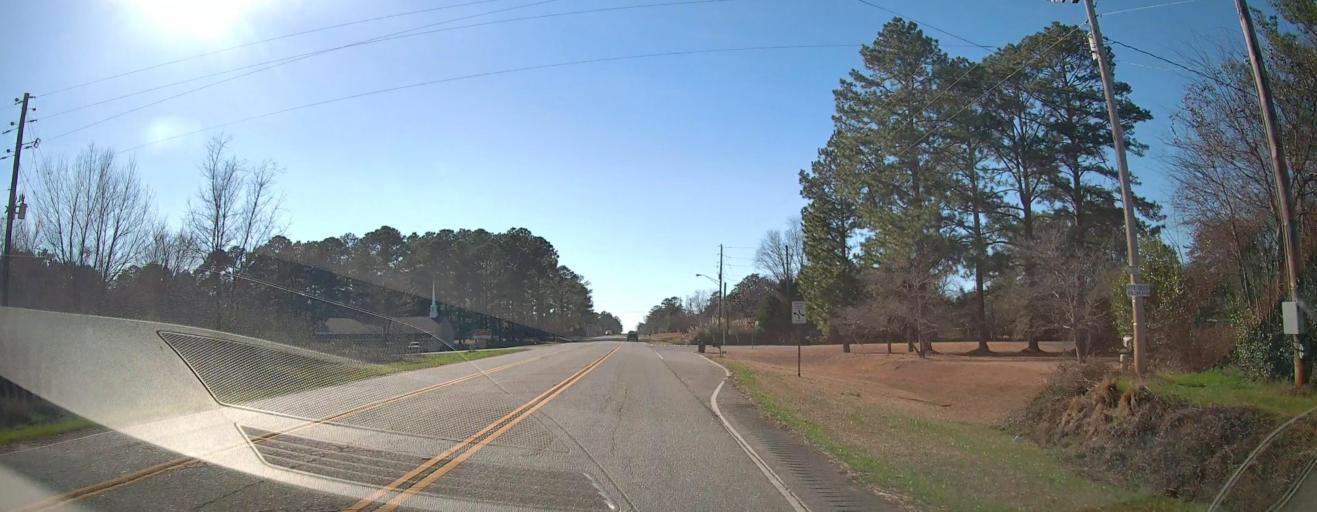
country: US
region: Georgia
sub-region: Sumter County
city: Americus
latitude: 32.0710
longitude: -84.1921
